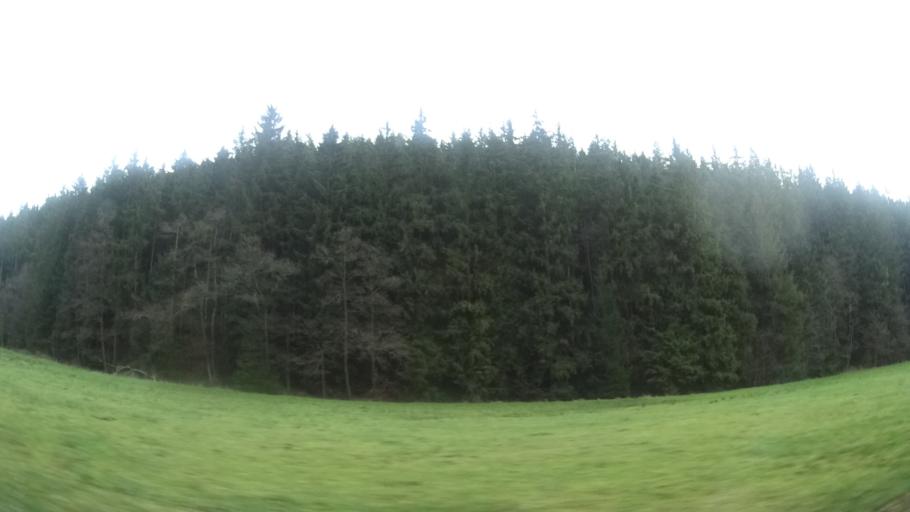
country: DE
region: Thuringia
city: Wittgendorf
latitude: 50.5948
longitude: 11.2358
